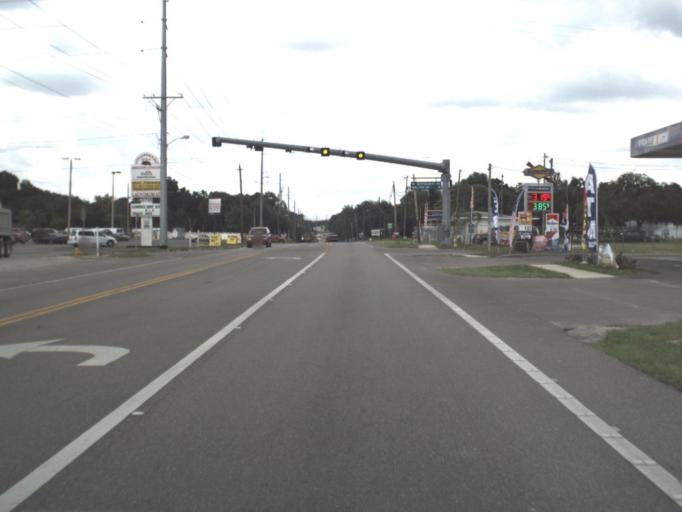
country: US
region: Florida
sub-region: Hillsborough County
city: Plant City
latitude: 28.0196
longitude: -82.1589
